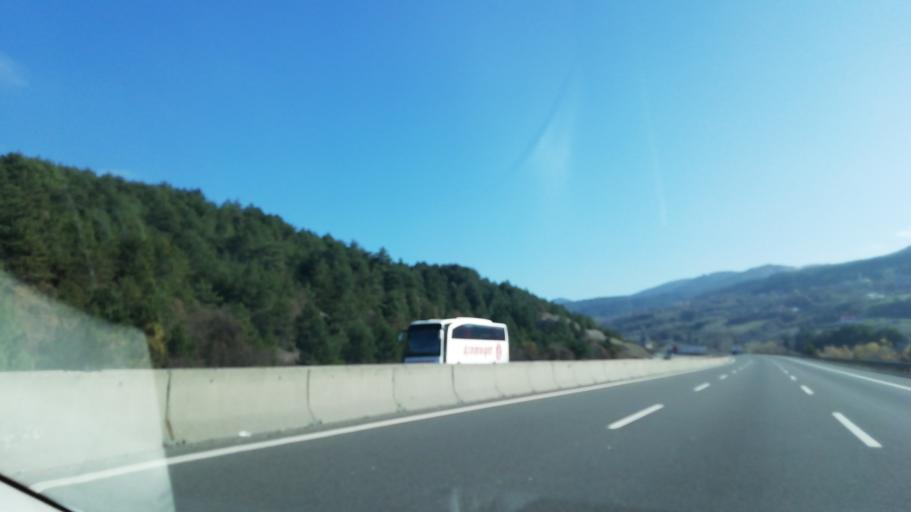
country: TR
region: Bolu
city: Bolu
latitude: 40.7357
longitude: 31.8009
